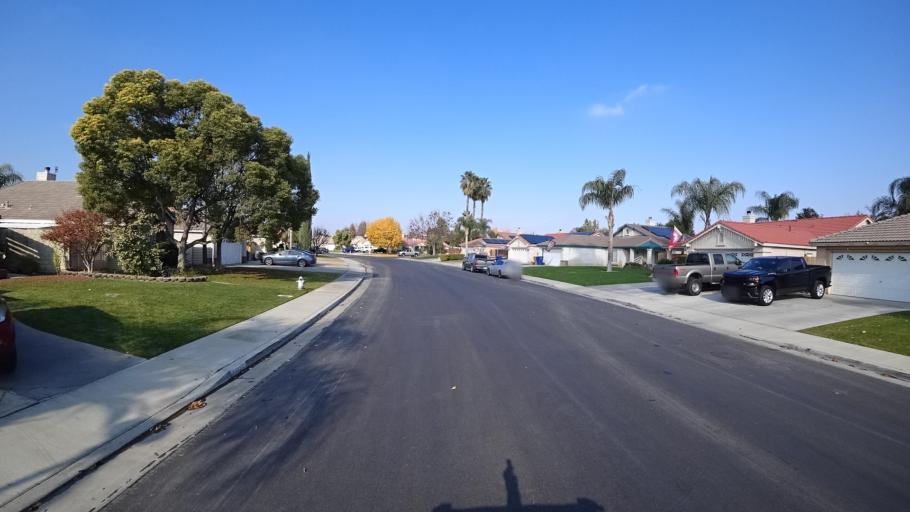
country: US
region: California
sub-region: Kern County
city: Greenacres
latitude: 35.3061
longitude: -119.0807
